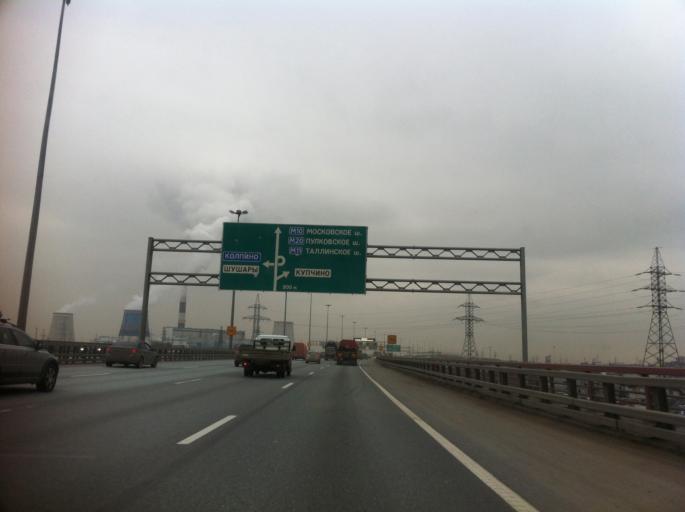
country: RU
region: St.-Petersburg
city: Obukhovo
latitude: 59.8418
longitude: 30.4554
